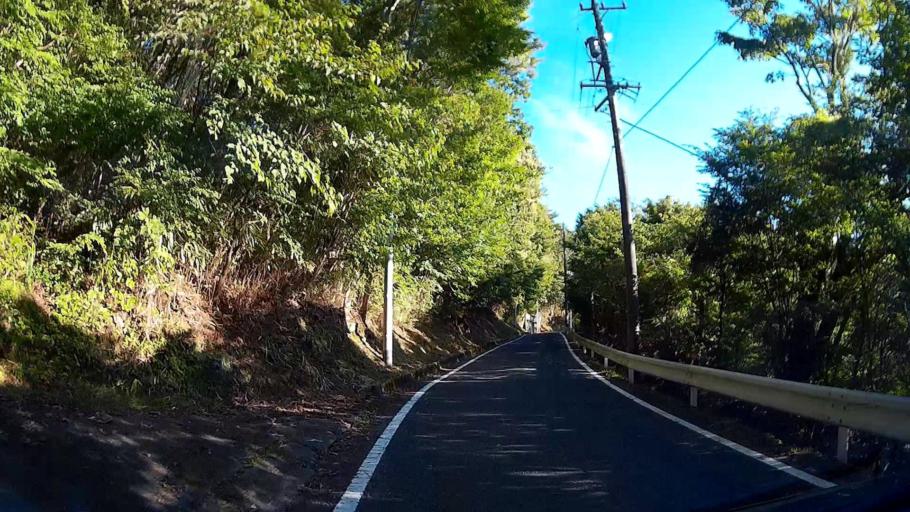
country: JP
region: Shizuoka
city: Shizuoka-shi
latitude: 35.1987
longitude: 138.2526
